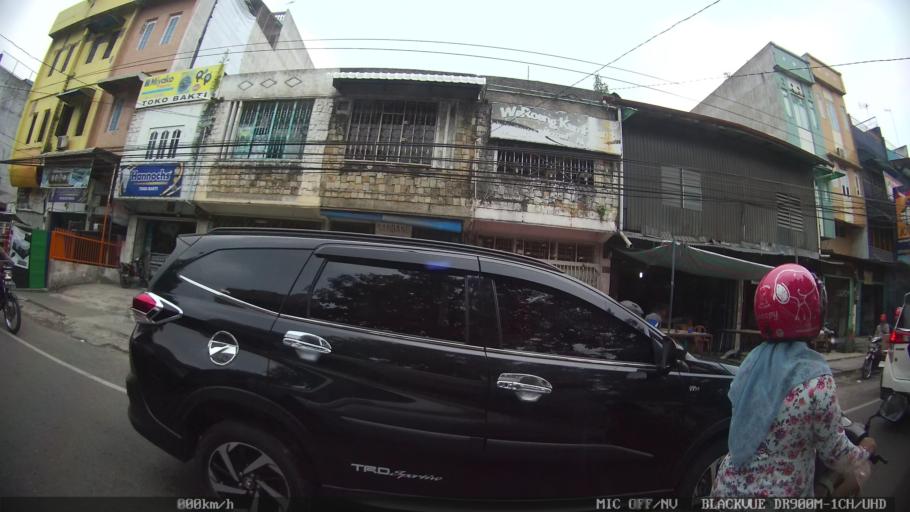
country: ID
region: North Sumatra
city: Medan
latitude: 3.5814
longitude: 98.7038
